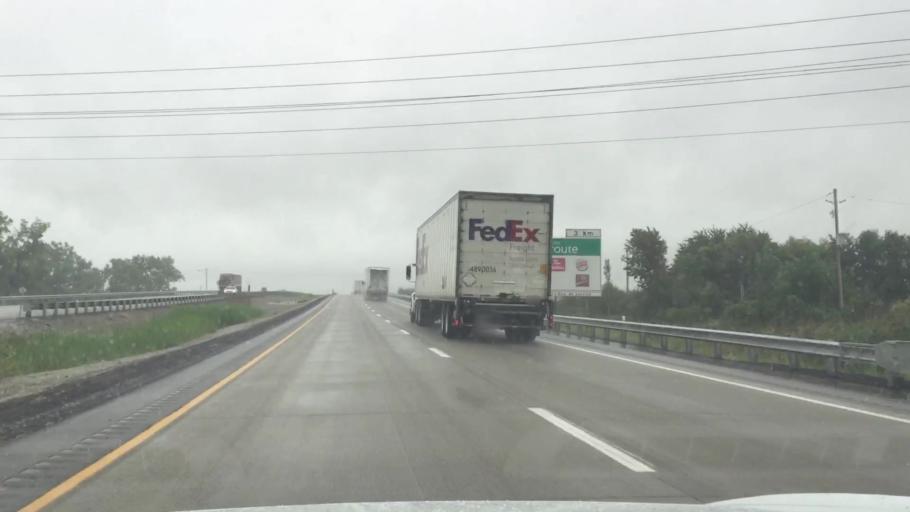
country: CA
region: Ontario
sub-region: Lambton County
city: Walpole Island
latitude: 42.2696
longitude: -82.4358
